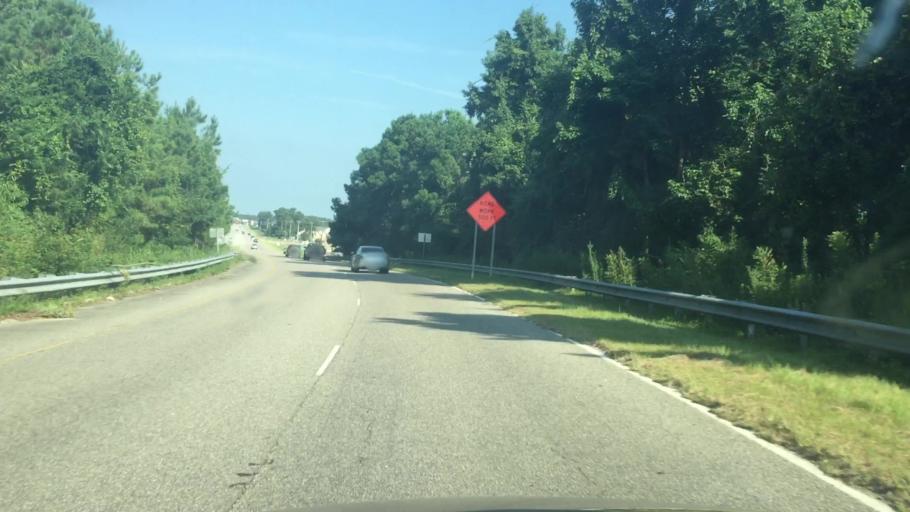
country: US
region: South Carolina
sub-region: Horry County
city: Little River
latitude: 33.8641
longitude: -78.6580
